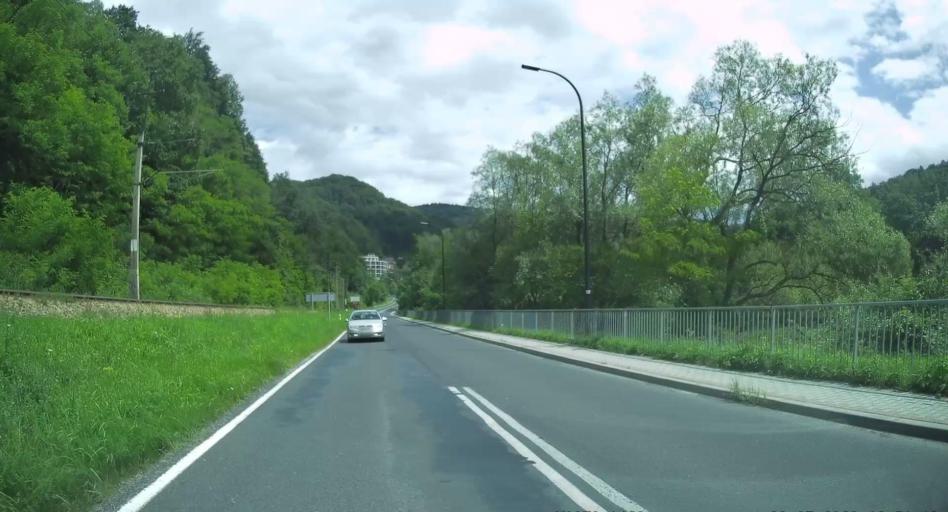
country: PL
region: Lesser Poland Voivodeship
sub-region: Powiat nowosadecki
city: Muszyna
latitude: 49.3637
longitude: 20.7977
